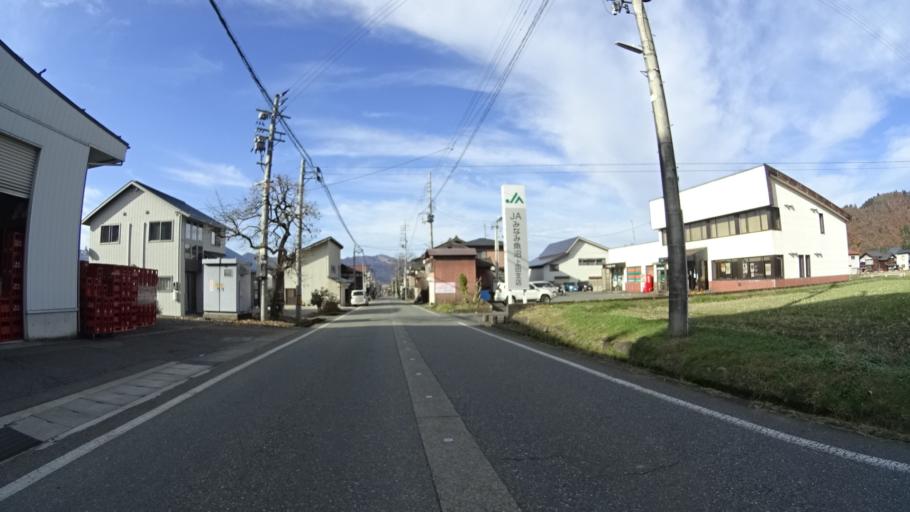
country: JP
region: Niigata
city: Shiozawa
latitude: 37.0157
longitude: 138.8787
